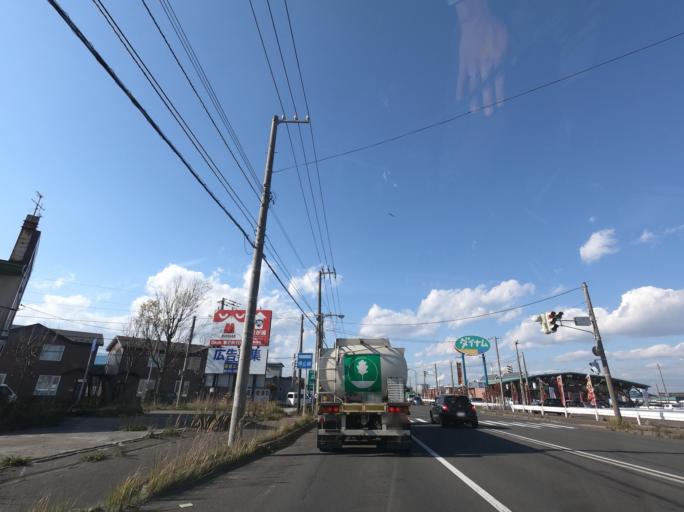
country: JP
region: Hokkaido
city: Kushiro
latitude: 42.9950
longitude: 144.3672
